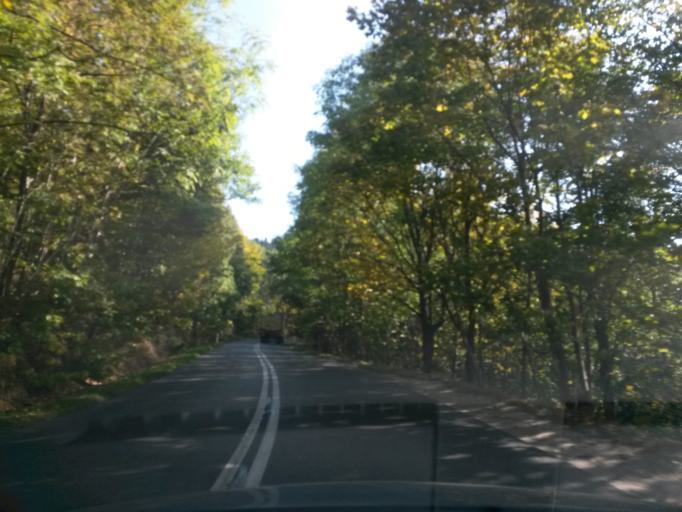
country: PL
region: Lower Silesian Voivodeship
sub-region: Powiat jeleniogorski
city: Kowary
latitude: 50.7674
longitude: 15.8603
